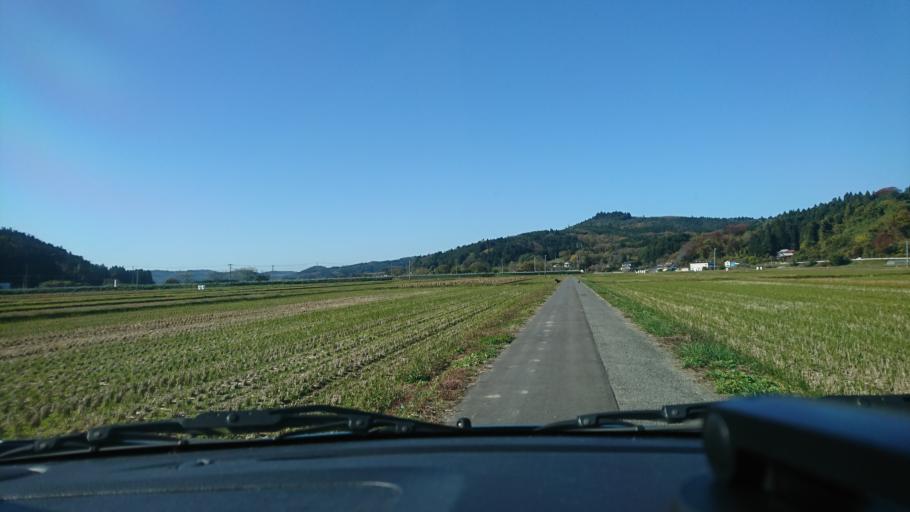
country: JP
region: Iwate
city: Ichinoseki
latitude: 38.8527
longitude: 141.2857
